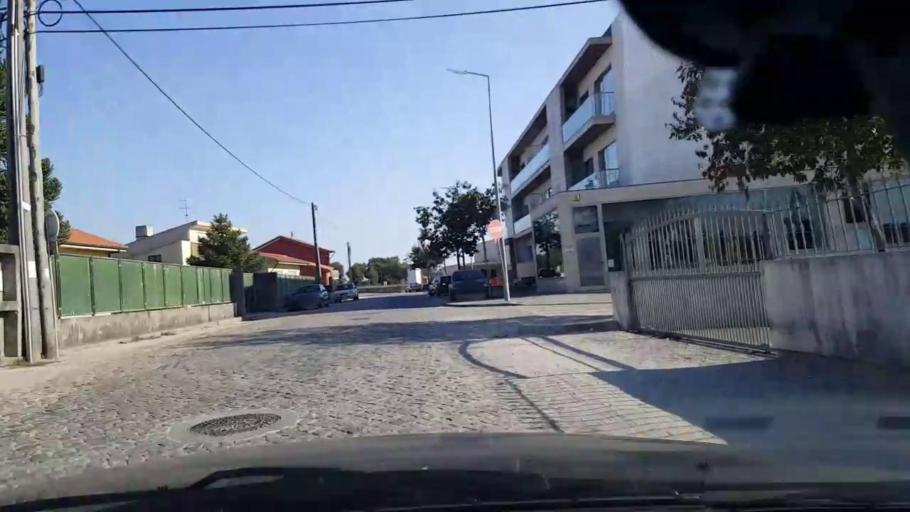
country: PT
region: Porto
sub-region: Vila do Conde
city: Arvore
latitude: 41.3524
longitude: -8.7204
